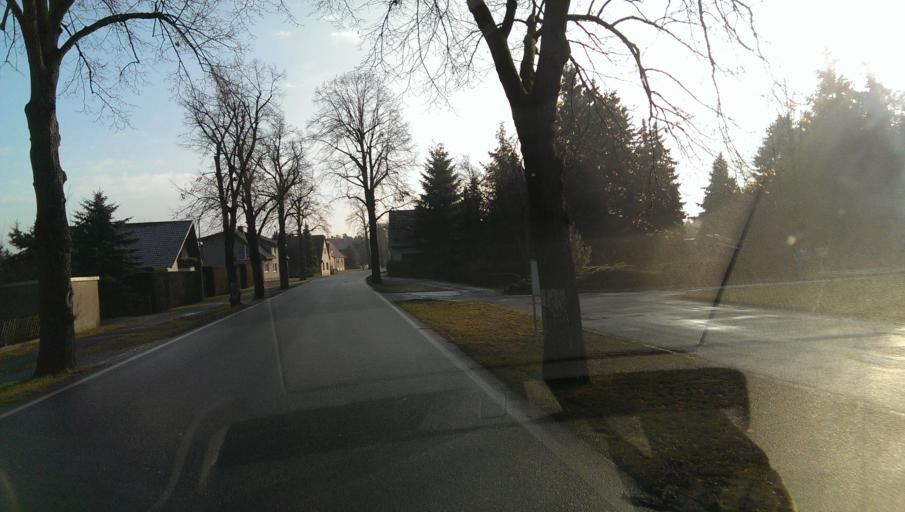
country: DE
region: Brandenburg
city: Bad Liebenwerda
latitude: 51.5503
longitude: 13.3816
